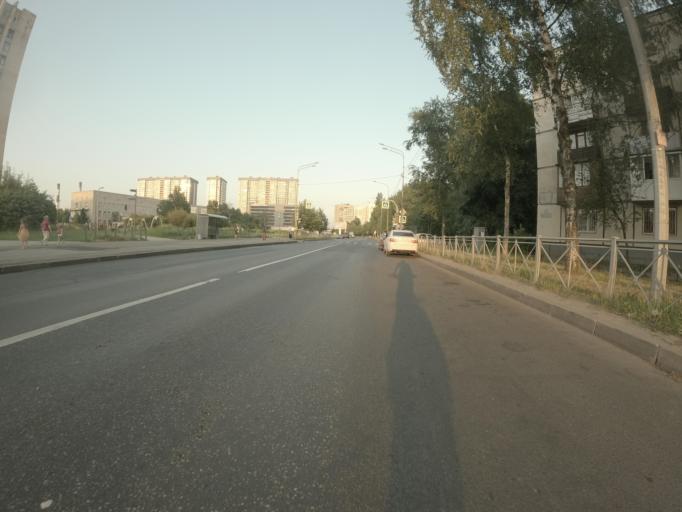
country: RU
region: Leningrad
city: Kalininskiy
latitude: 59.9780
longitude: 30.4293
